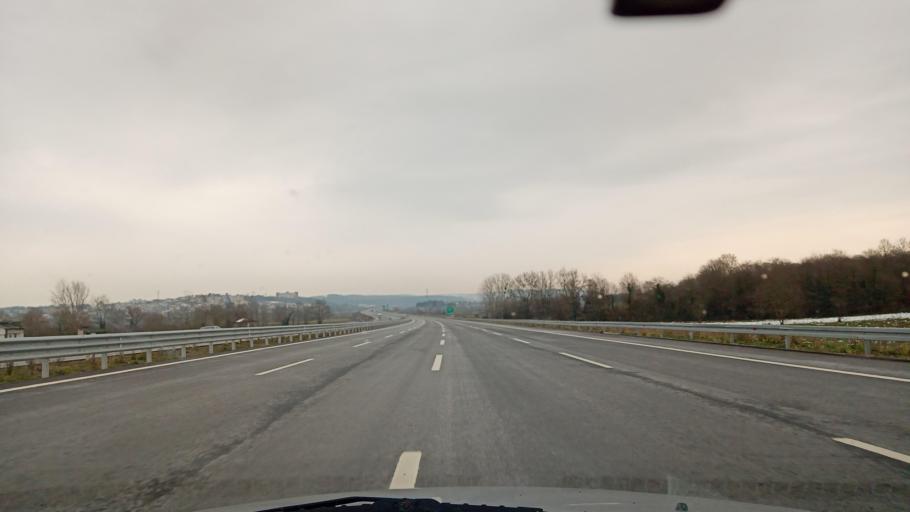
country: TR
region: Sakarya
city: Kazimpasa
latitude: 40.8431
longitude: 30.3062
